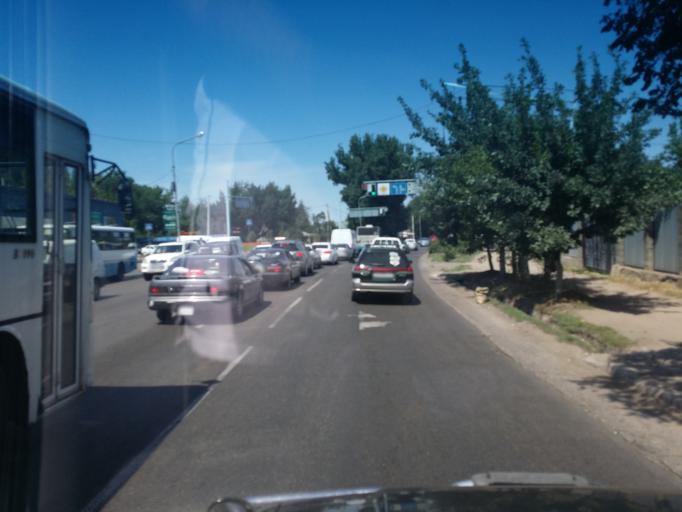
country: KZ
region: Almaty Qalasy
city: Almaty
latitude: 43.3001
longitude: 76.9303
